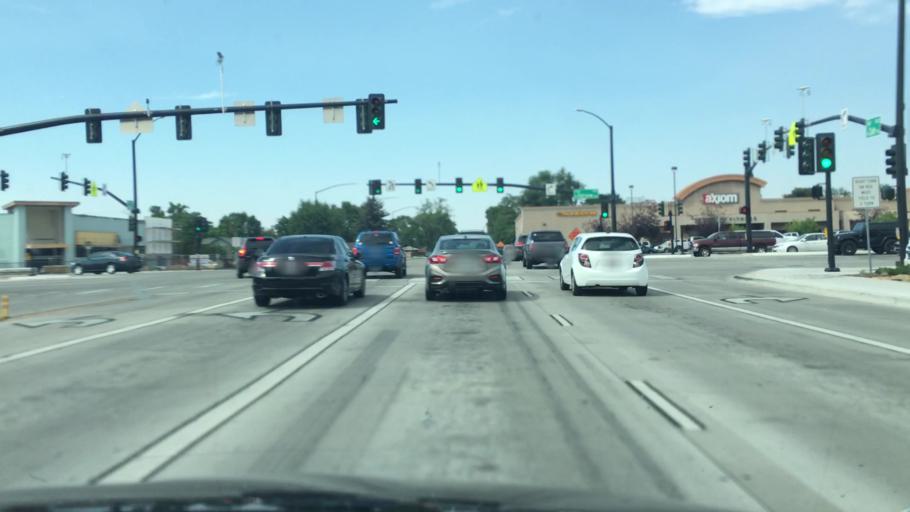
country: US
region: Idaho
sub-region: Ada County
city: Garden City
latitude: 43.6189
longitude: -116.2742
